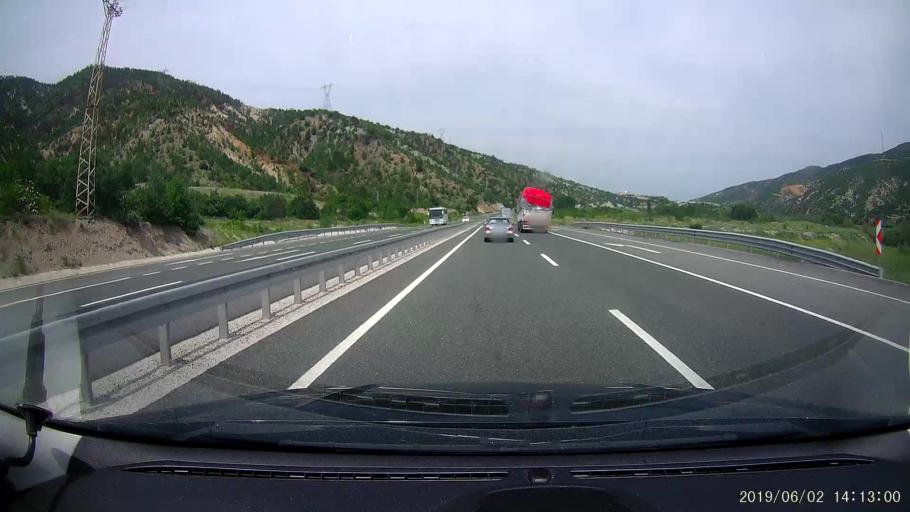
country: TR
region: Cankiri
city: Yaprakli
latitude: 40.9217
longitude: 33.8198
